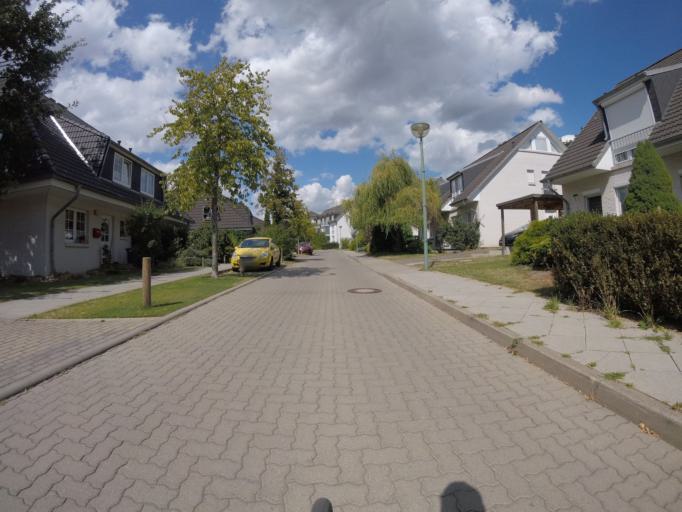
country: DE
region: Brandenburg
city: Werder
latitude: 52.4111
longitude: 12.9941
